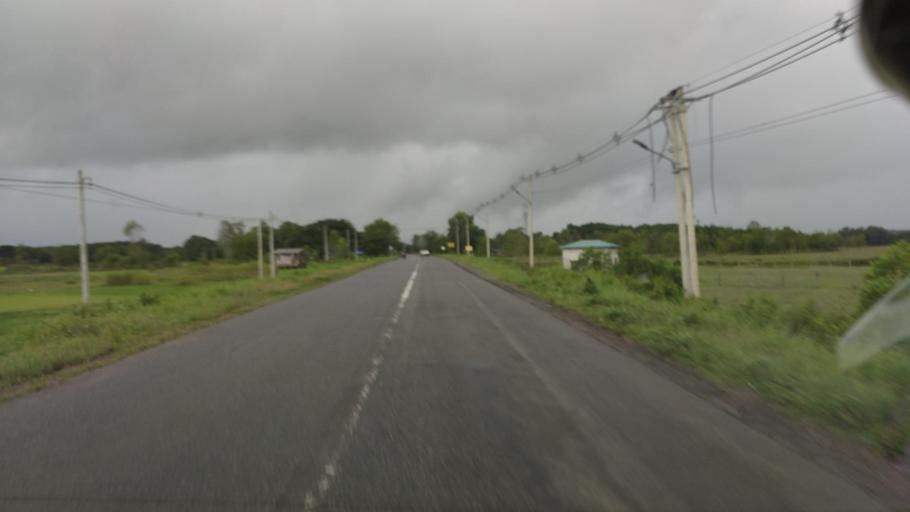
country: MM
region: Bago
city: Bago
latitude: 17.3671
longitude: 96.4641
